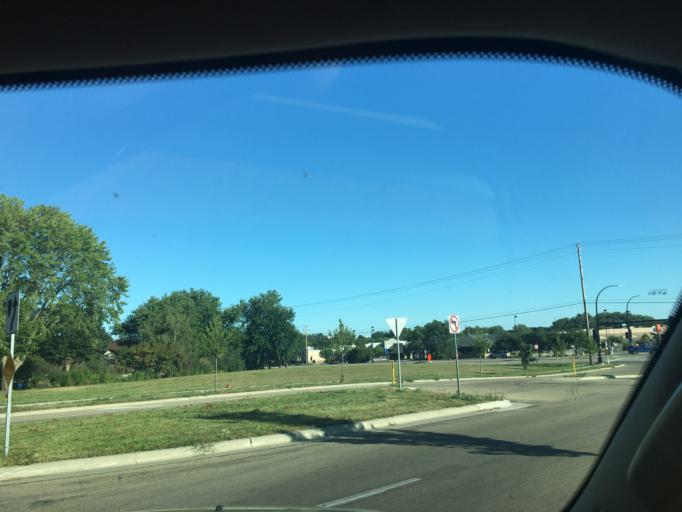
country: US
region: Minnesota
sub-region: Olmsted County
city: Rochester
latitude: 44.0807
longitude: -92.5148
